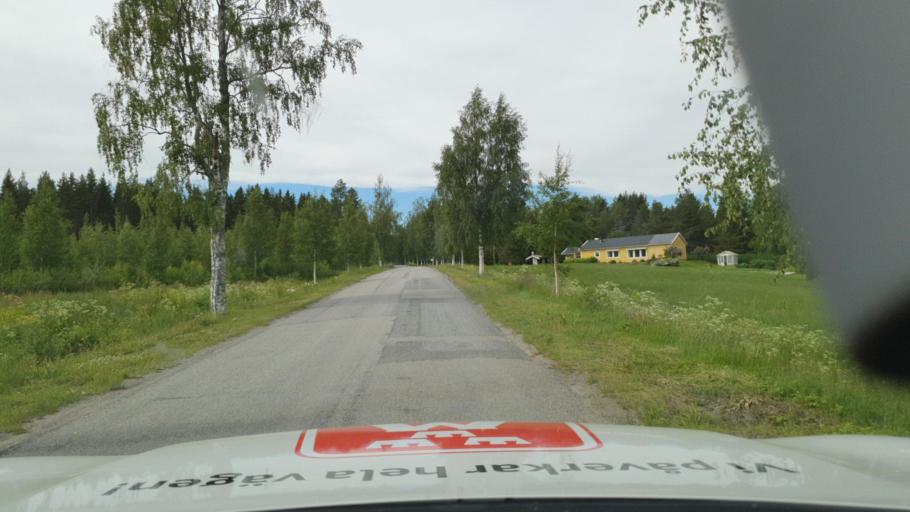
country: SE
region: Vaesterbotten
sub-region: Skelleftea Kommun
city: Burtraesk
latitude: 64.4328
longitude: 20.5146
